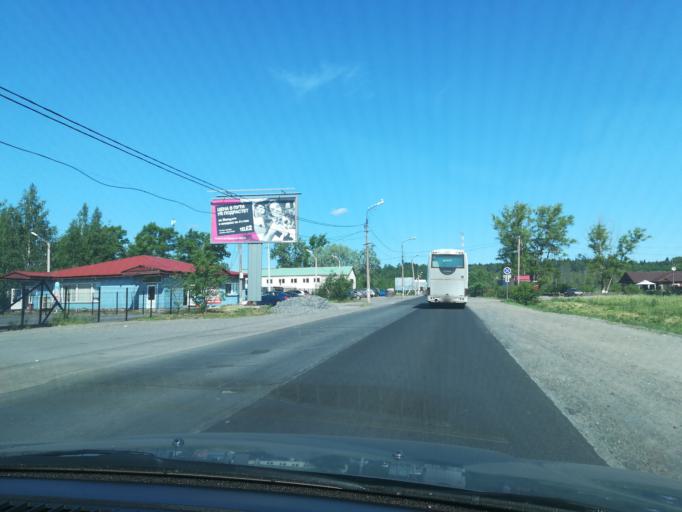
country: RU
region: Leningrad
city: Svetogorsk
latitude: 61.1164
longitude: 28.8508
